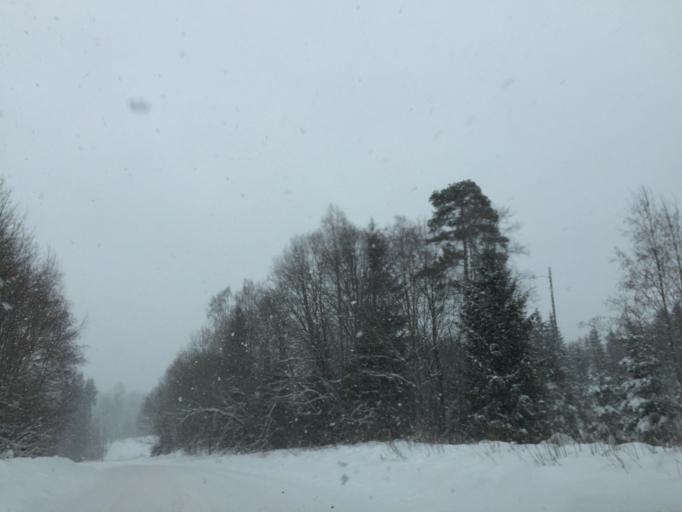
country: LV
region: Amatas Novads
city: Drabesi
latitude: 57.0766
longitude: 25.3415
